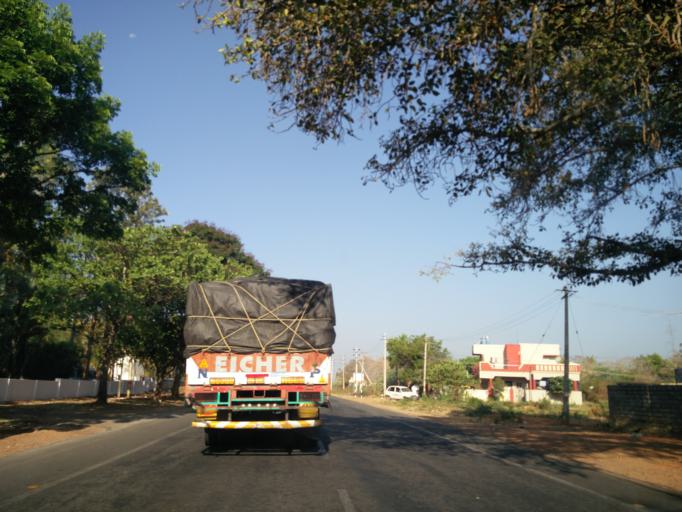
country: IN
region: Karnataka
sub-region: Tumkur
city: Tumkur
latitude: 13.3418
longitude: 77.0388
